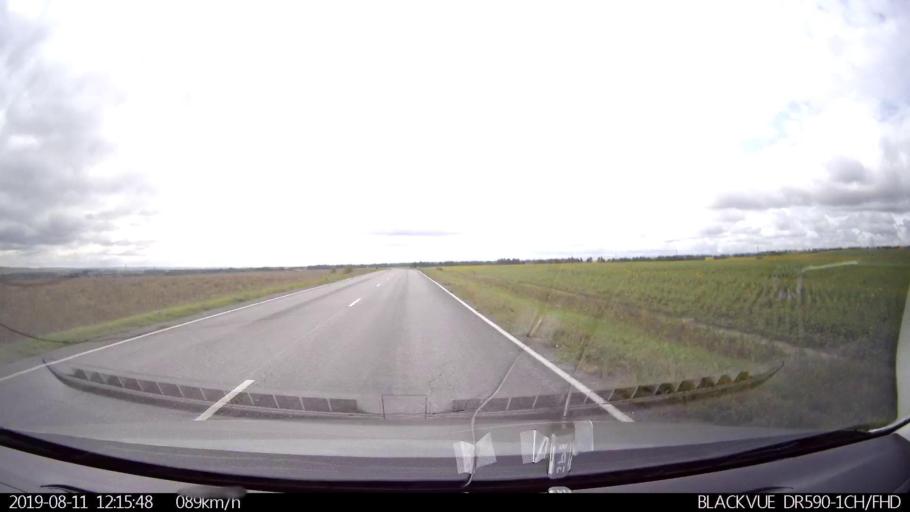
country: RU
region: Ulyanovsk
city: Ignatovka
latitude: 53.9377
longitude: 47.9649
